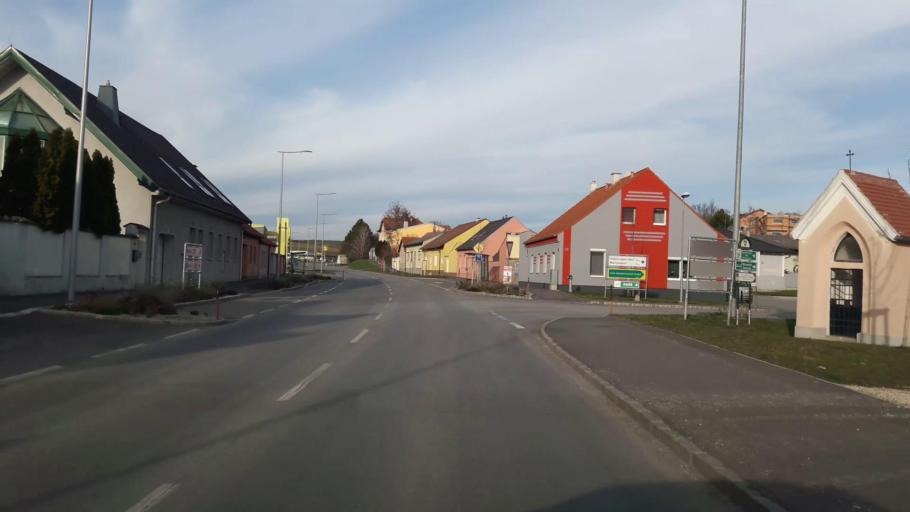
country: AT
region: Lower Austria
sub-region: Politischer Bezirk Mistelbach
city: Gaweinstal
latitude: 48.4810
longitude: 16.5935
